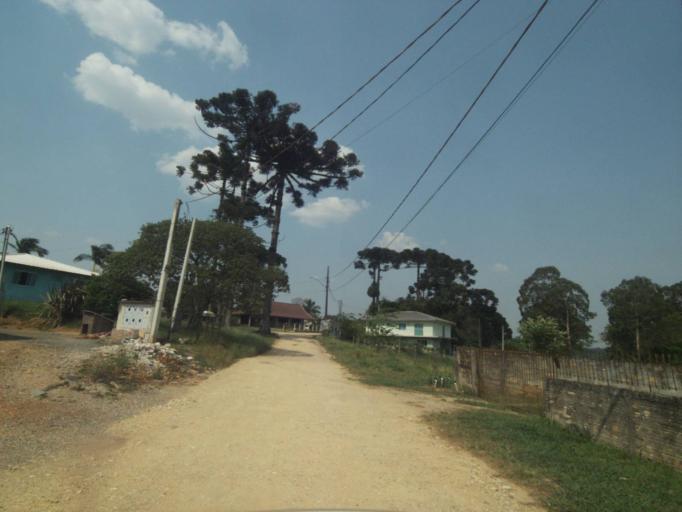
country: BR
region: Parana
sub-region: Sao Jose Dos Pinhais
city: Sao Jose dos Pinhais
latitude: -25.5560
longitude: -49.2296
